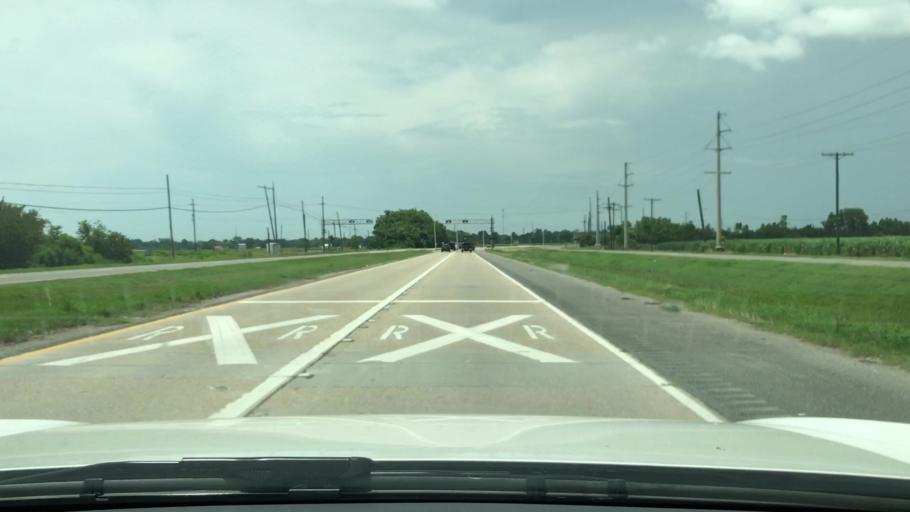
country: US
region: Louisiana
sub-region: West Baton Rouge Parish
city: Addis
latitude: 30.3380
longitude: -91.2594
